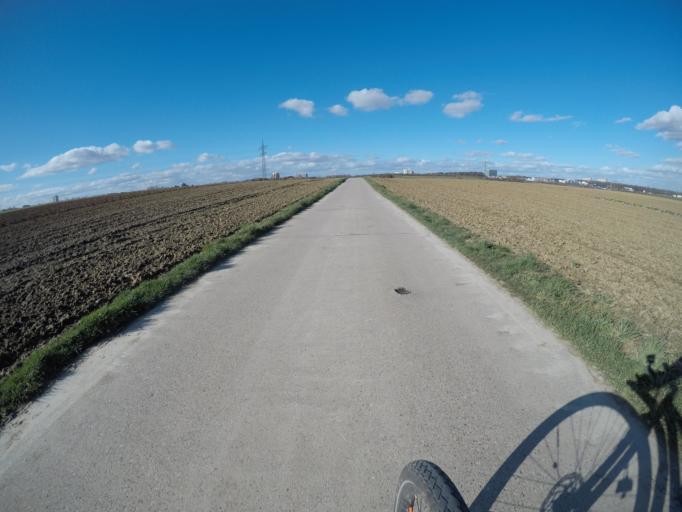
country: DE
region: Baden-Wuerttemberg
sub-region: Regierungsbezirk Stuttgart
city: Leinfelden-Echterdingen
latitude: 48.6976
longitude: 9.1599
